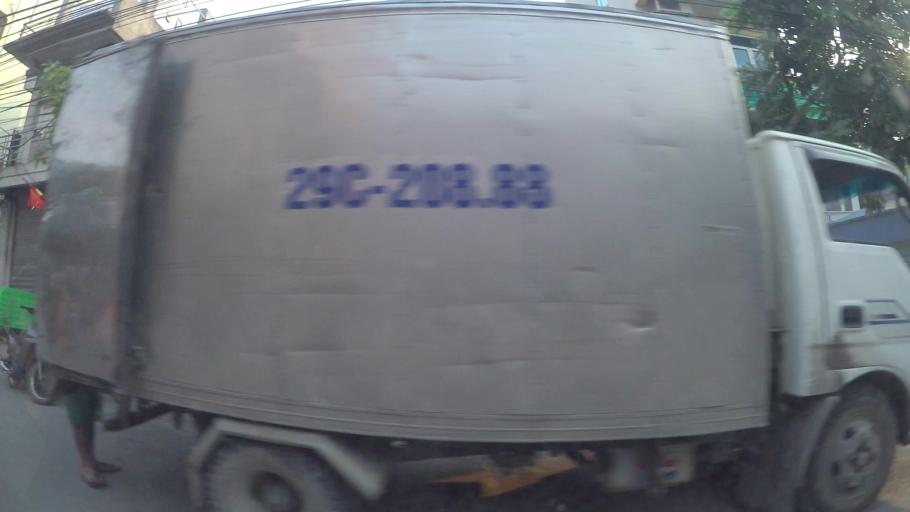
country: VN
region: Ha Noi
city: Van Dien
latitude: 20.9273
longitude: 105.8367
